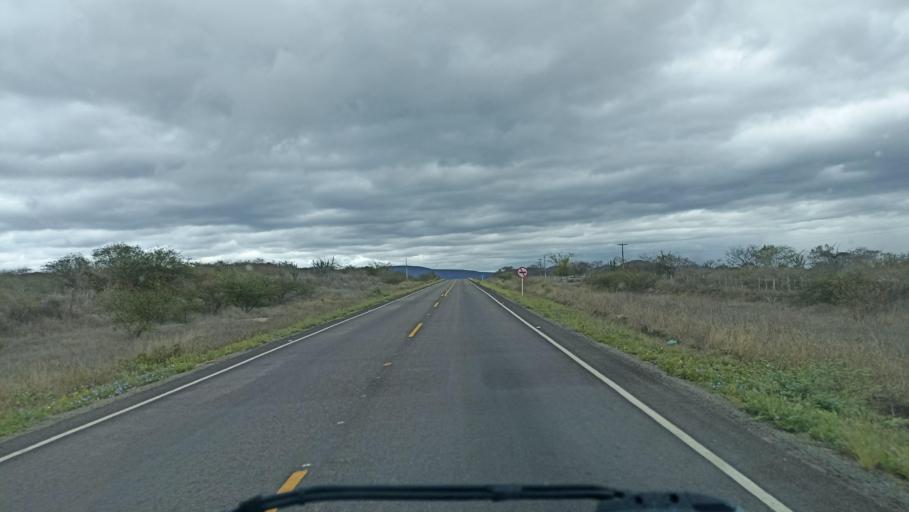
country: BR
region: Bahia
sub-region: Iacu
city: Iacu
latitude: -12.9095
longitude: -40.4077
